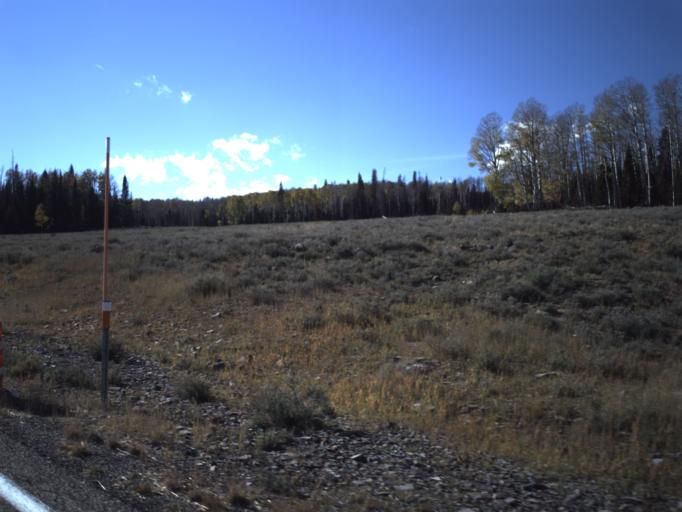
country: US
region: Utah
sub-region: Iron County
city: Parowan
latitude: 37.6614
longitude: -112.7330
